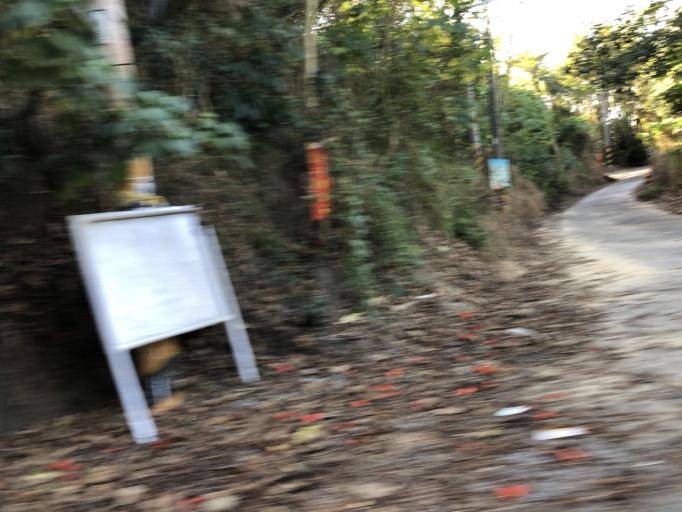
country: TW
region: Taiwan
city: Yujing
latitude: 23.0231
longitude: 120.3828
